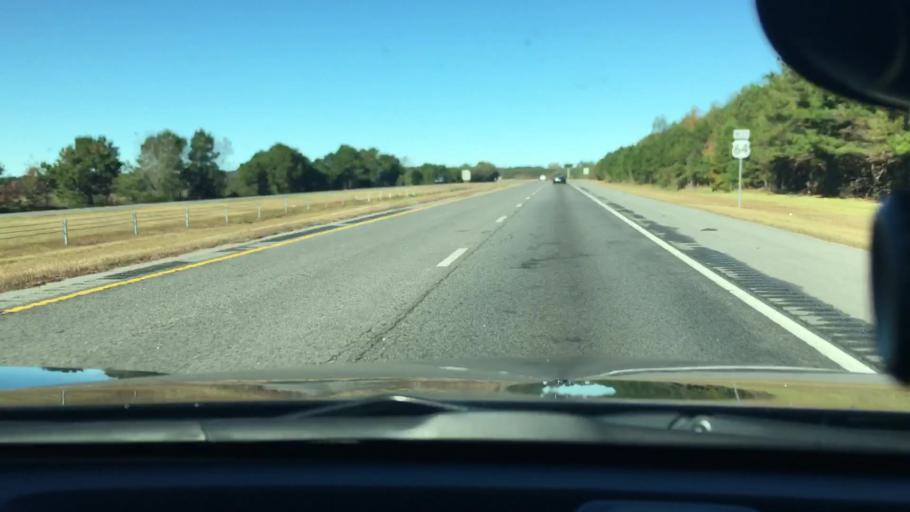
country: US
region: North Carolina
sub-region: Pitt County
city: Bethel
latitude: 35.8470
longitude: -77.4157
